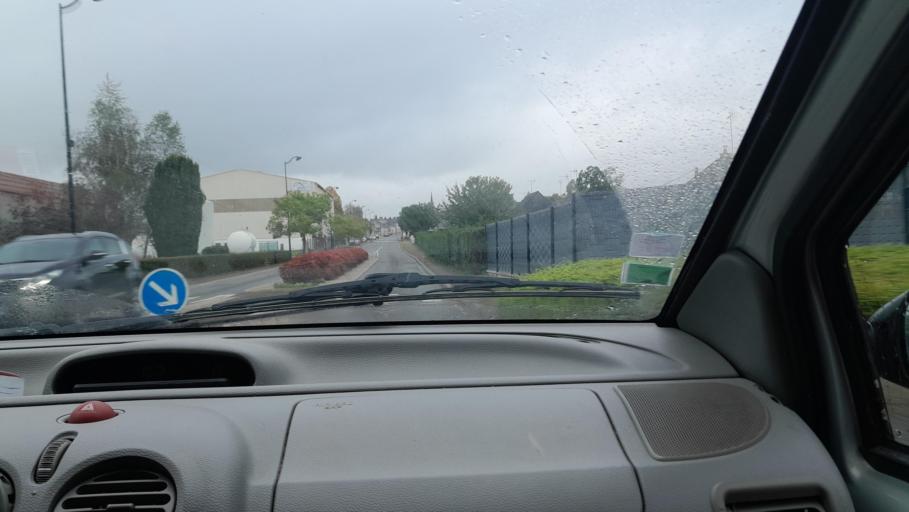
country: FR
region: Pays de la Loire
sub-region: Departement de la Mayenne
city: Congrier
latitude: 47.8369
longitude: -1.1392
